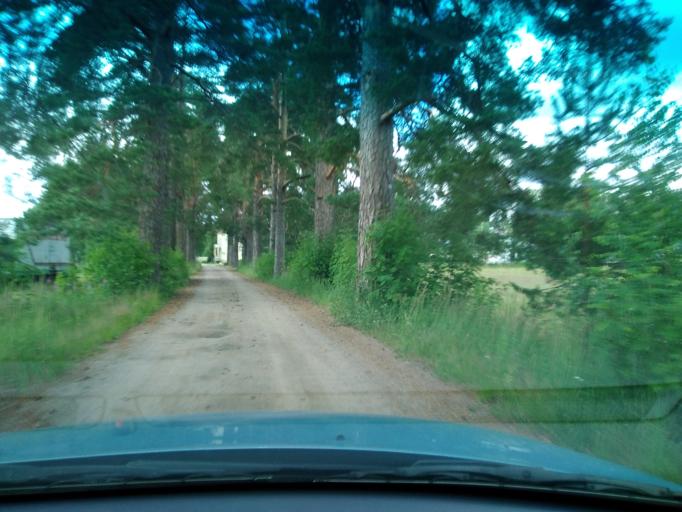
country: FI
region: Central Finland
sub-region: Saarijaervi-Viitasaari
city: Saarijaervi
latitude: 62.7371
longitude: 25.1825
